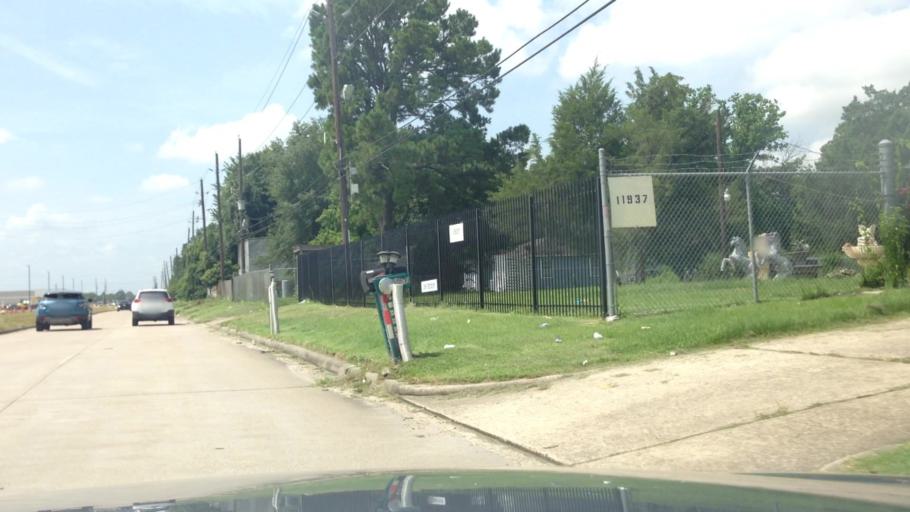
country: US
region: Texas
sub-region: Harris County
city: Jersey Village
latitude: 29.9474
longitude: -95.5470
